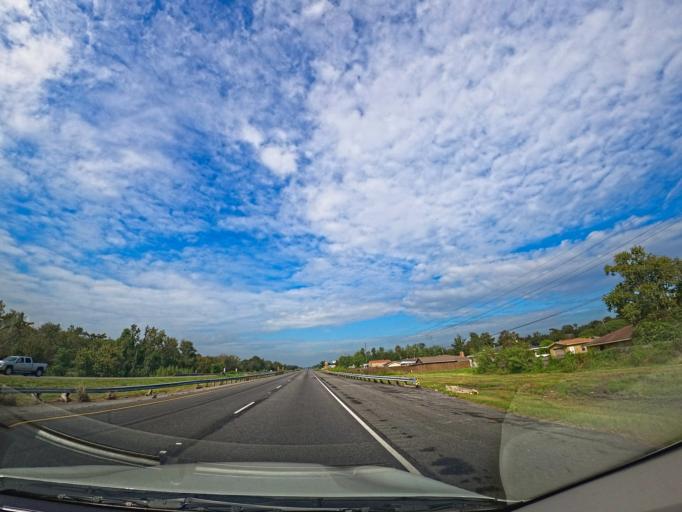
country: US
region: Louisiana
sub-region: Saint Mary Parish
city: Patterson
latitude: 29.6923
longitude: -91.3266
